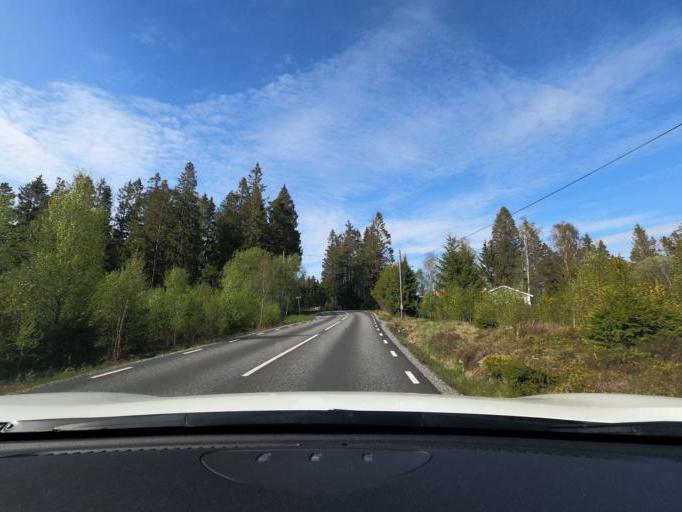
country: SE
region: Vaestra Goetaland
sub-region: Harryda Kommun
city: Landvetter
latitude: 57.6417
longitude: 12.2545
